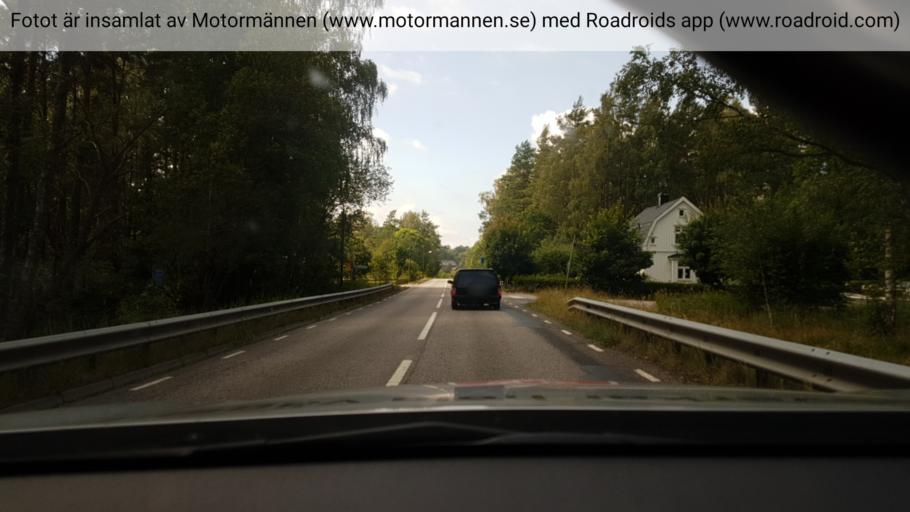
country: SE
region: Vaestra Goetaland
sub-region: Marks Kommun
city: Kinna
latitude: 57.4773
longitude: 12.7105
